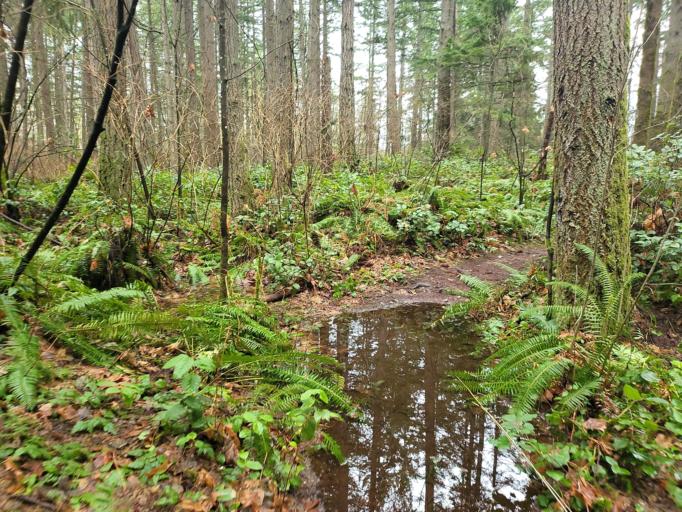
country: US
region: Washington
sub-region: King County
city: East Renton Highlands
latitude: 47.4801
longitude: -122.1445
